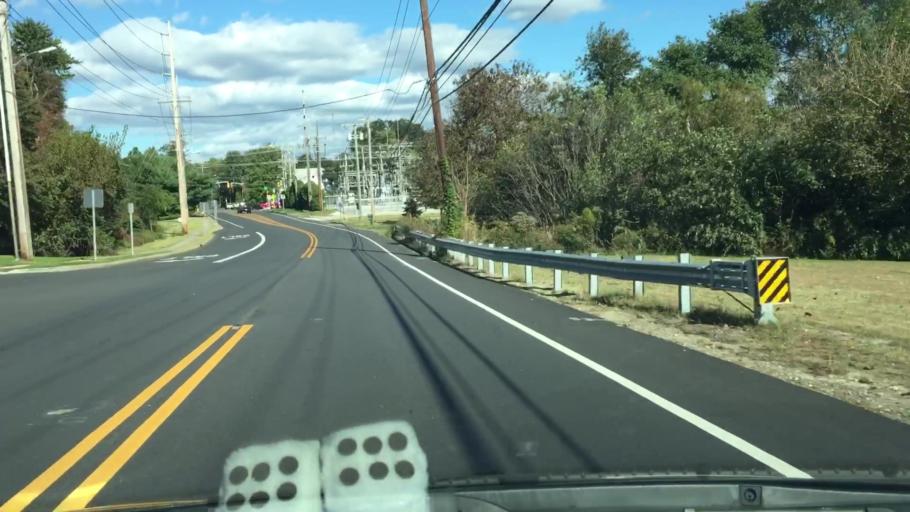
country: US
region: New Jersey
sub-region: Gloucester County
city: Turnersville
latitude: 39.7768
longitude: -75.0613
